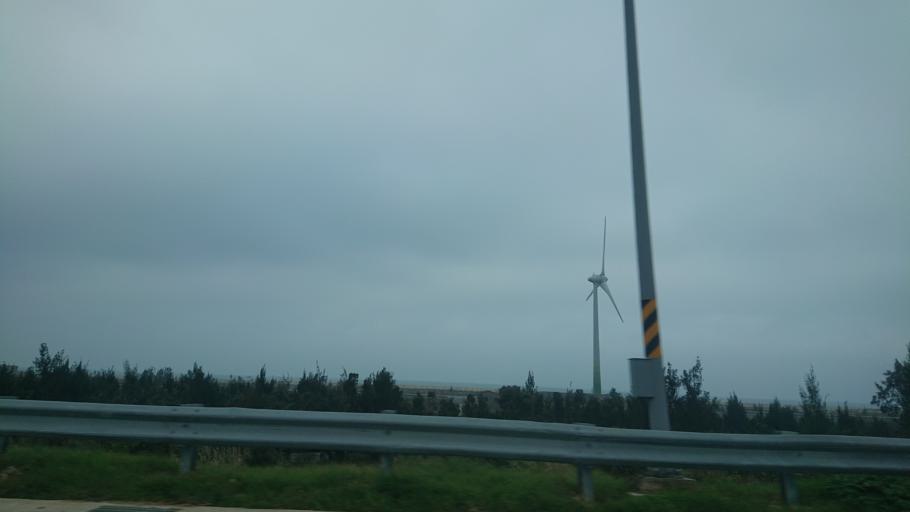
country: TW
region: Taiwan
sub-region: Miaoli
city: Miaoli
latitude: 24.5107
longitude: 120.6838
